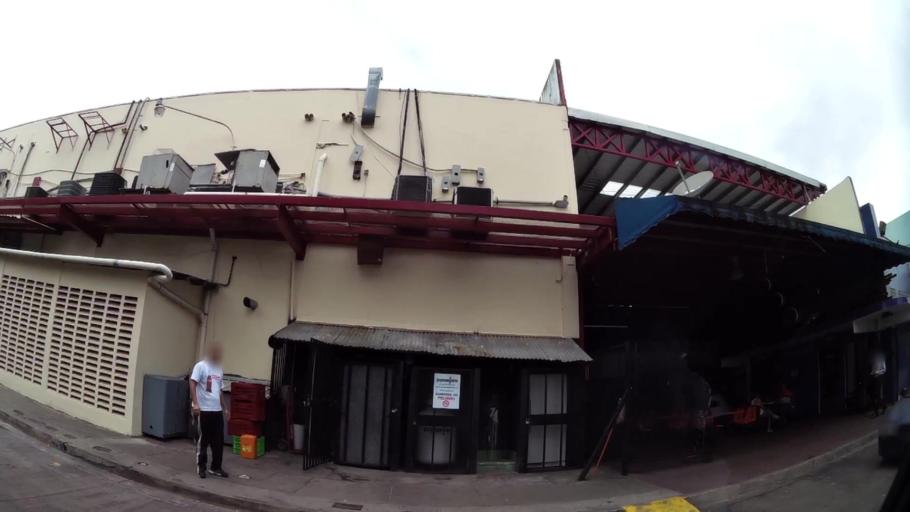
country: PA
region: Panama
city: San Miguelito
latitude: 9.0482
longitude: -79.4499
